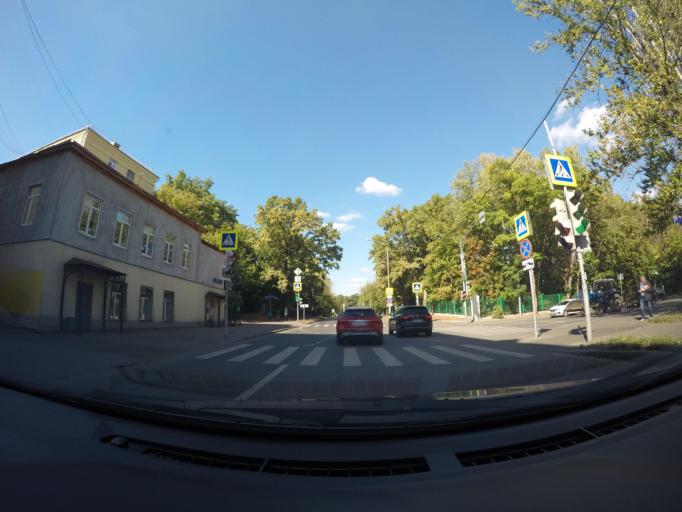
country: RU
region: Moscow
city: Sokol'niki
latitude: 55.7980
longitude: 37.6884
